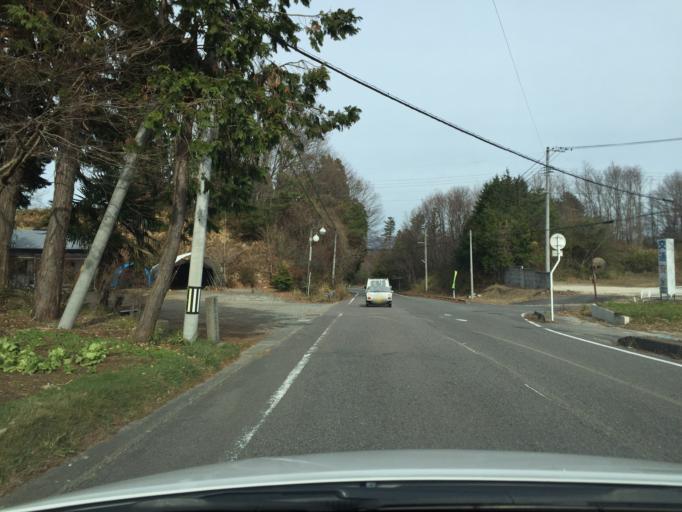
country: JP
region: Fukushima
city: Funehikimachi-funehiki
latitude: 37.3883
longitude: 140.5910
